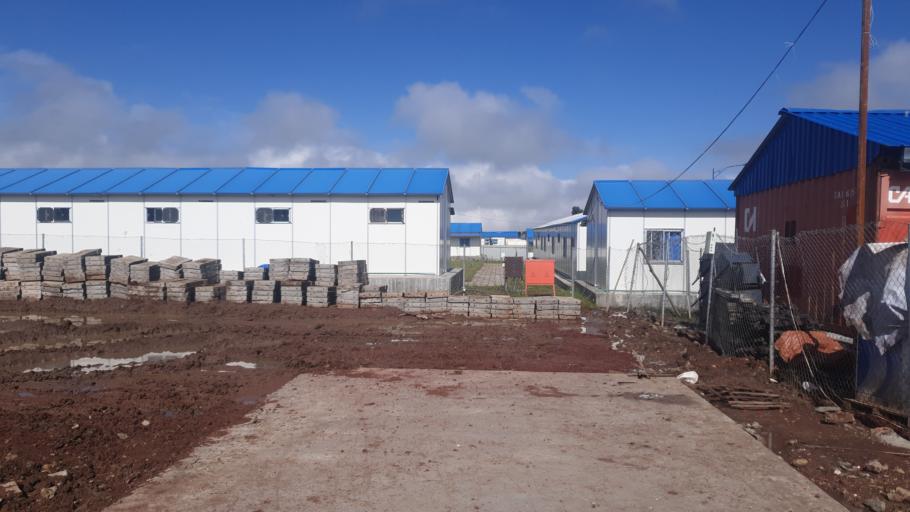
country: ET
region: Oromiya
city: Ziway
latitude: 7.5291
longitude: 38.9694
